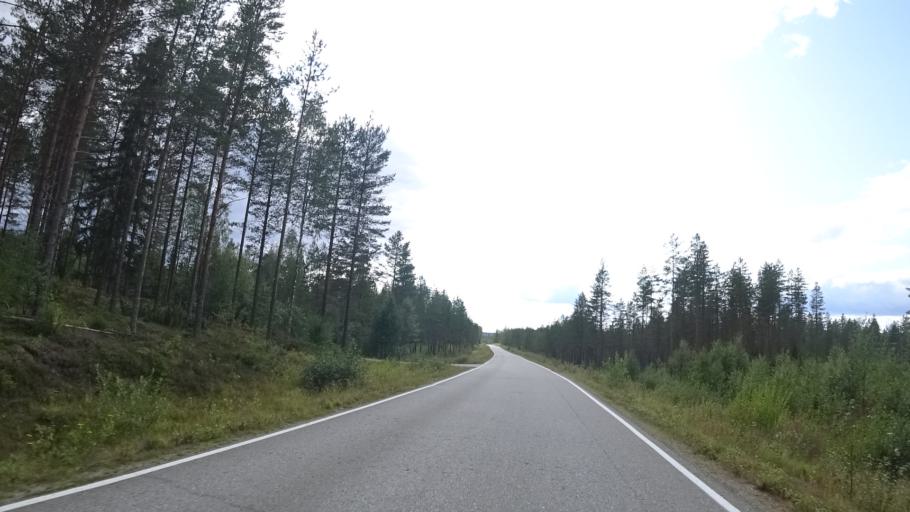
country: FI
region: North Karelia
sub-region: Joensuu
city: Ilomantsi
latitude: 62.4201
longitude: 31.0195
